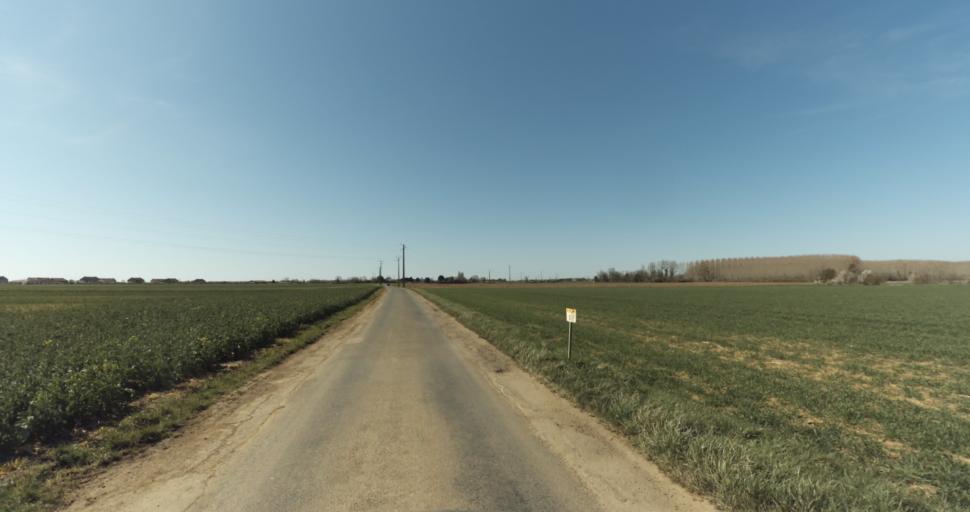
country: FR
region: Lower Normandy
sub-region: Departement du Calvados
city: Saint-Pierre-sur-Dives
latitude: 49.0507
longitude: -0.0384
